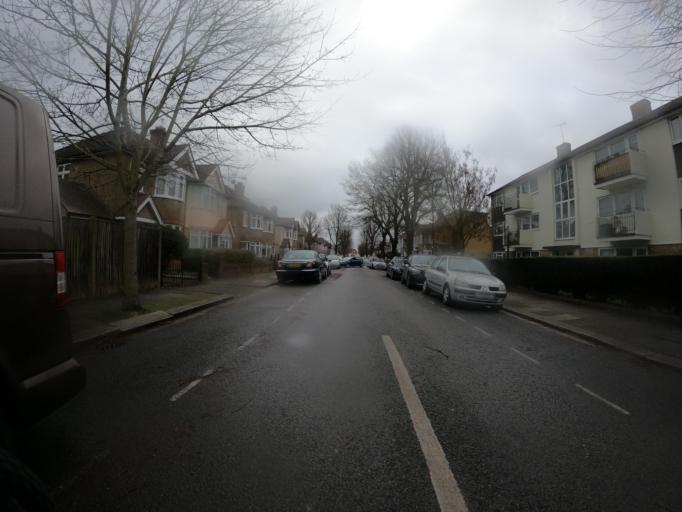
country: GB
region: England
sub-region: Greater London
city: Brentford
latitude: 51.4986
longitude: -0.3257
